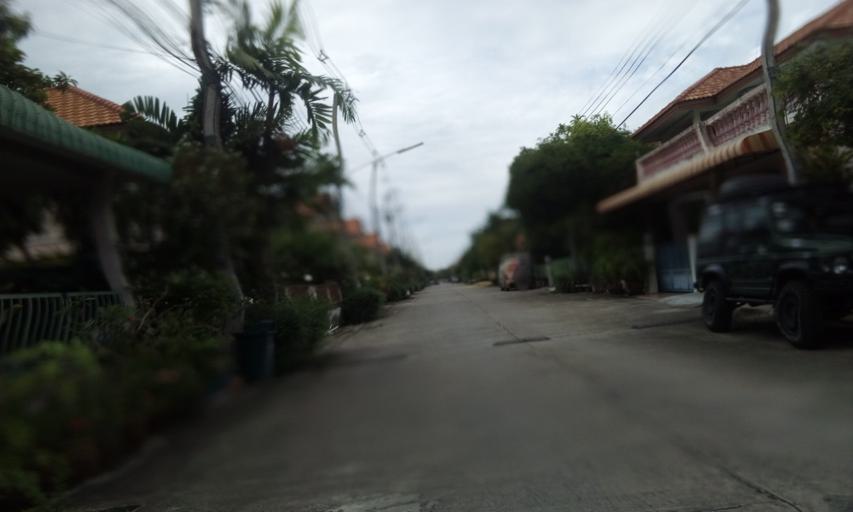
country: TH
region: Pathum Thani
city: Nong Suea
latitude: 14.0541
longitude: 100.8353
